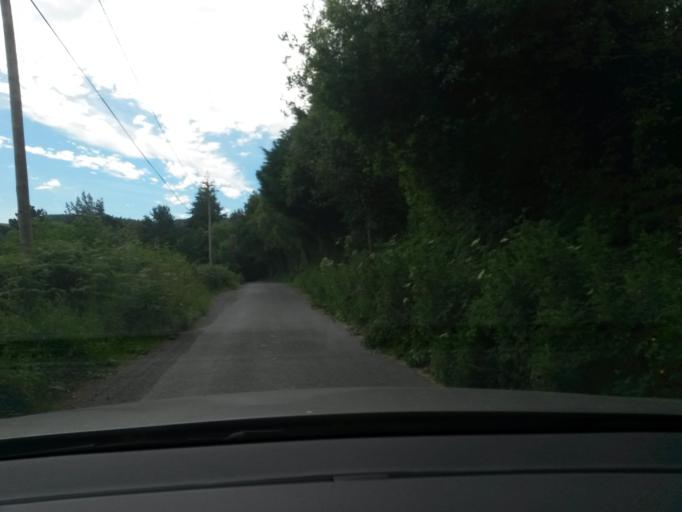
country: IE
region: Leinster
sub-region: Wicklow
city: Enniskerry
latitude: 53.1603
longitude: -6.2033
